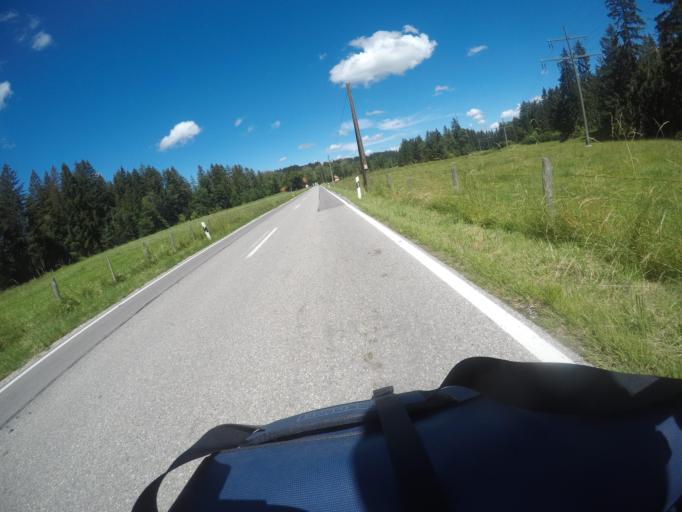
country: DE
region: Bavaria
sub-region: Upper Bavaria
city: Prem
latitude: 47.6589
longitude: 10.7858
